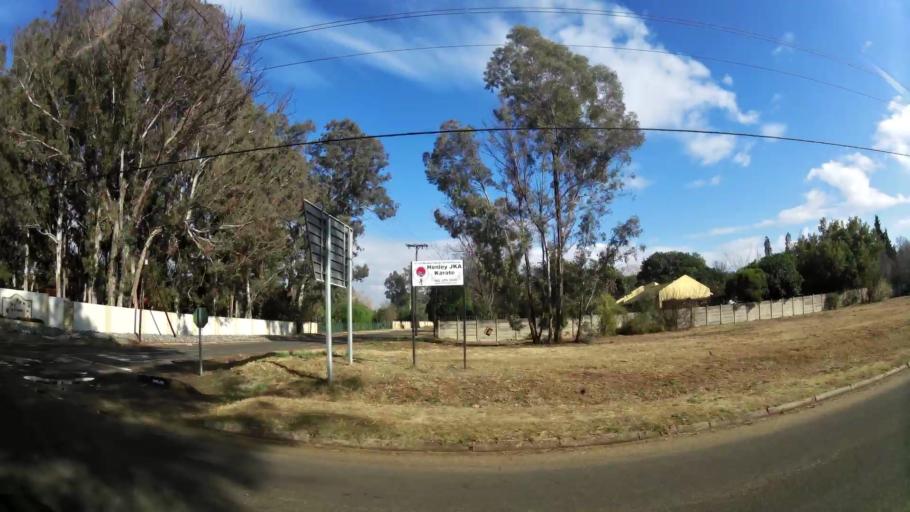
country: ZA
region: Gauteng
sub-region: Sedibeng District Municipality
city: Meyerton
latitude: -26.5437
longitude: 28.0617
